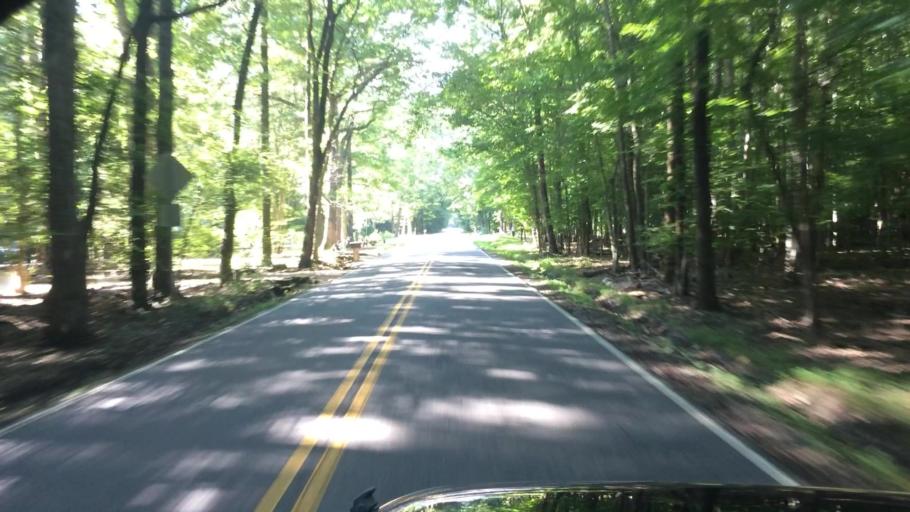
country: US
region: Virginia
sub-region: James City County
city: Williamsburg
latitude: 37.2449
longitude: -76.7956
